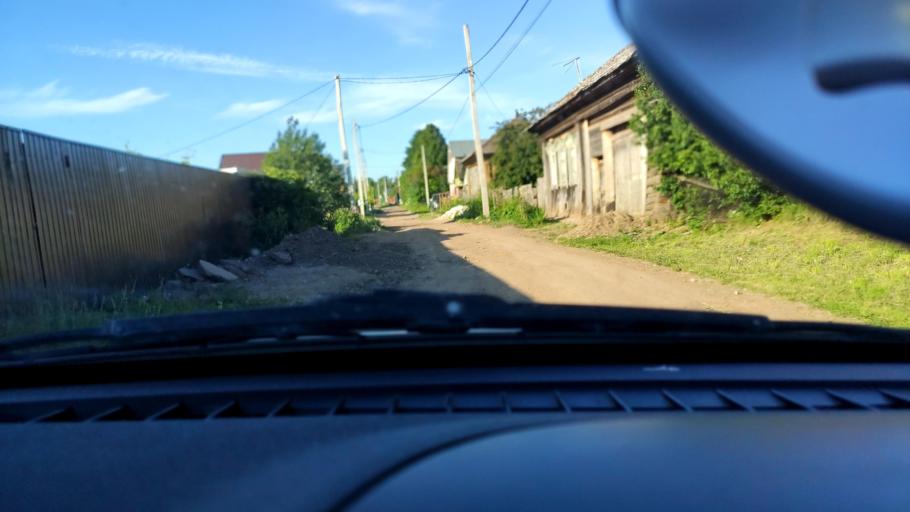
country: RU
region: Perm
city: Ferma
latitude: 57.9172
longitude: 56.3294
